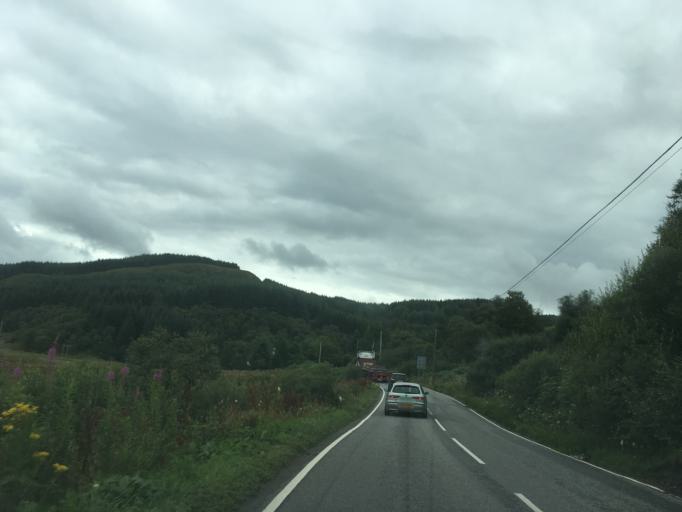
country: GB
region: Scotland
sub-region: Argyll and Bute
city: Oban
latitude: 56.3010
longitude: -5.4644
